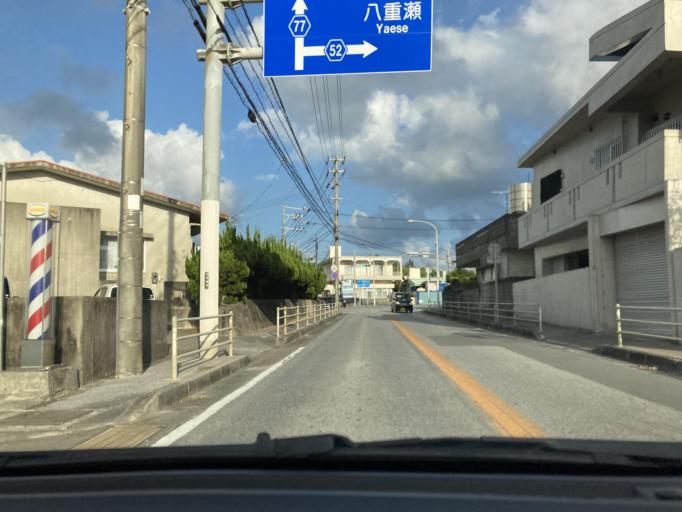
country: JP
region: Okinawa
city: Itoman
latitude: 26.1372
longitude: 127.6977
